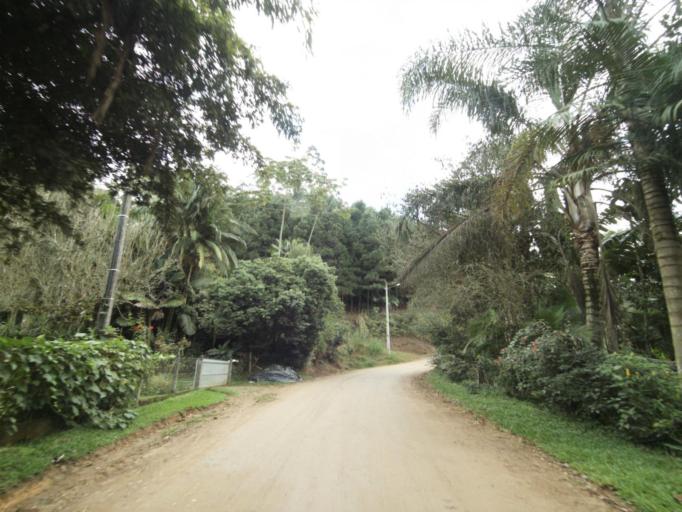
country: BR
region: Santa Catarina
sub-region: Pomerode
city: Pomerode
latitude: -26.7026
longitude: -49.2208
